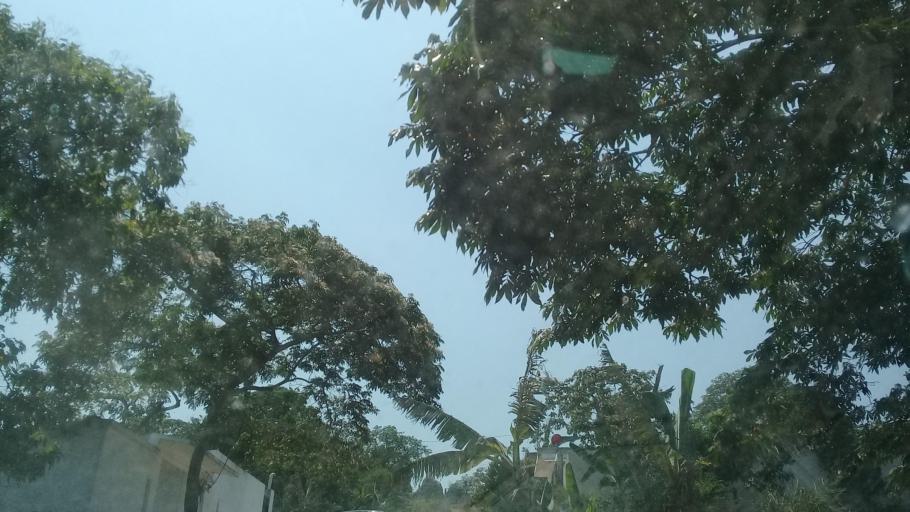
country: MX
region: Veracruz
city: El Castillo
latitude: 19.5669
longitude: -96.8445
